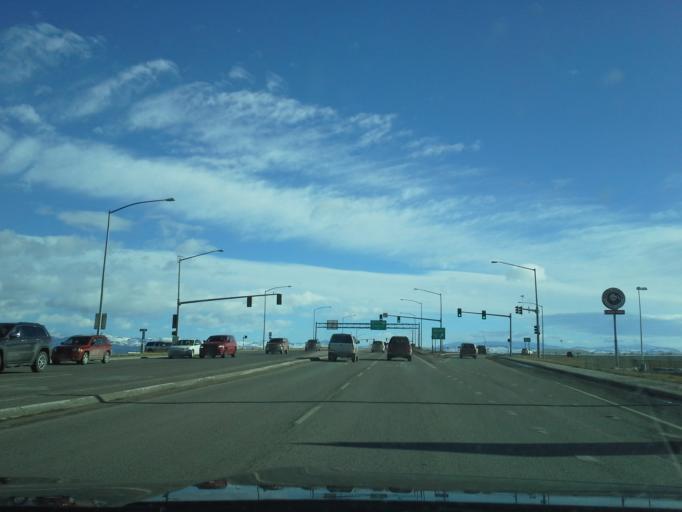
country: US
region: Montana
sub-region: Lewis and Clark County
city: Helena
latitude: 46.6165
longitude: -112.0150
